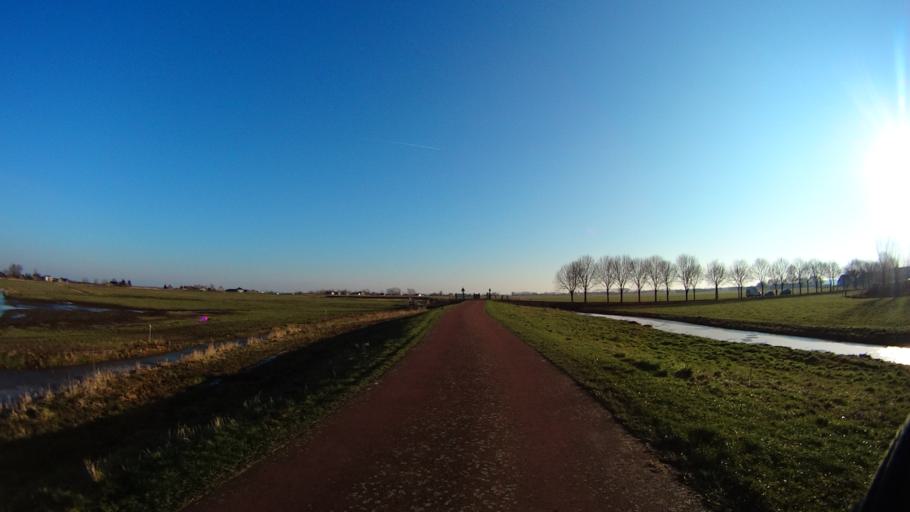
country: NL
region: Utrecht
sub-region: Gemeente Baarn
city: Baarn
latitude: 52.2459
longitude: 5.3042
